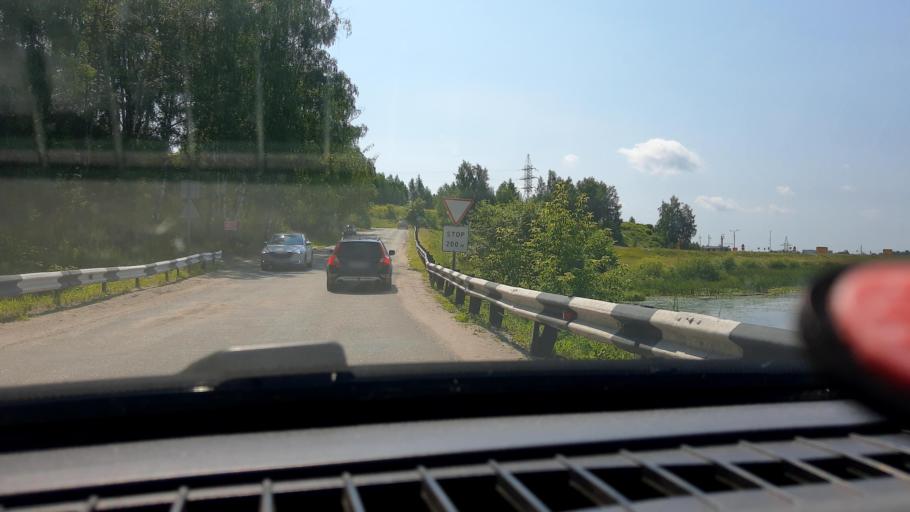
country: RU
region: Nizjnij Novgorod
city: Gorodets
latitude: 56.6877
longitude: 43.4299
